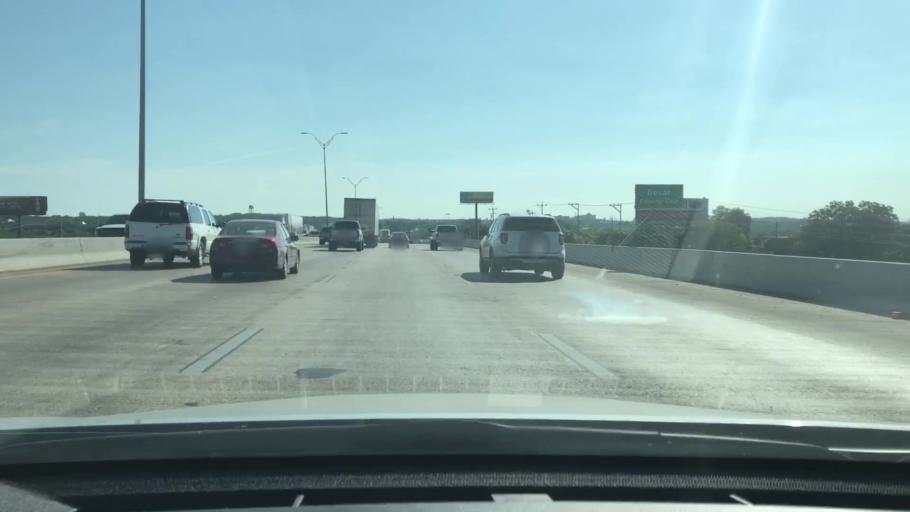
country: US
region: Texas
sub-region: Bexar County
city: Selma
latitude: 29.5858
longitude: -98.3041
